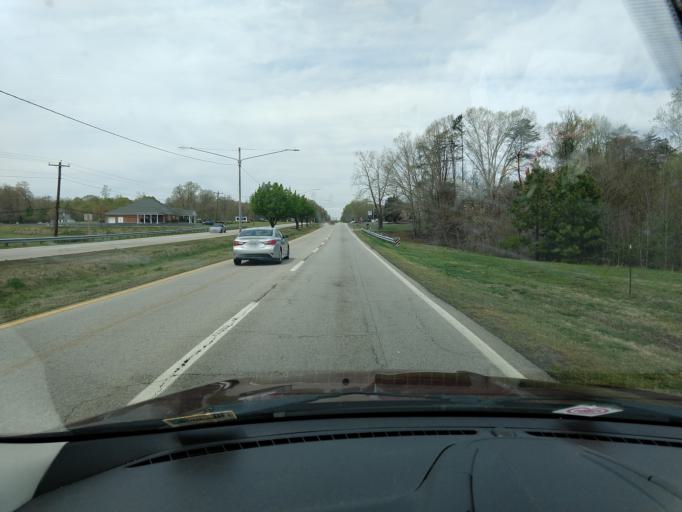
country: US
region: Virginia
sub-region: City of Danville
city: Danville
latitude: 36.5915
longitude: -79.4602
